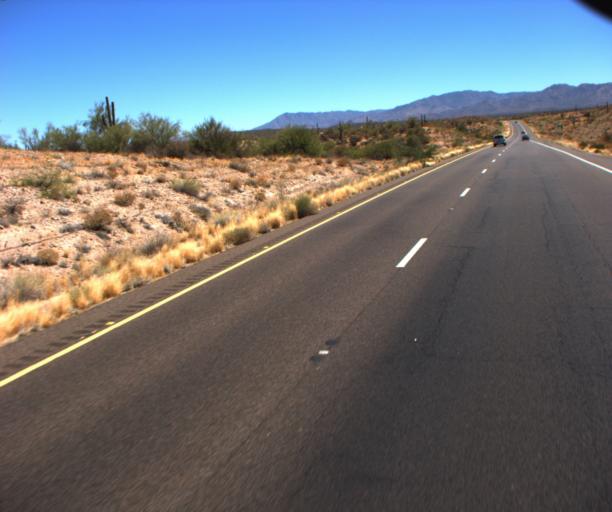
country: US
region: Arizona
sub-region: Maricopa County
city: Rio Verde
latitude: 33.6315
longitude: -111.5534
